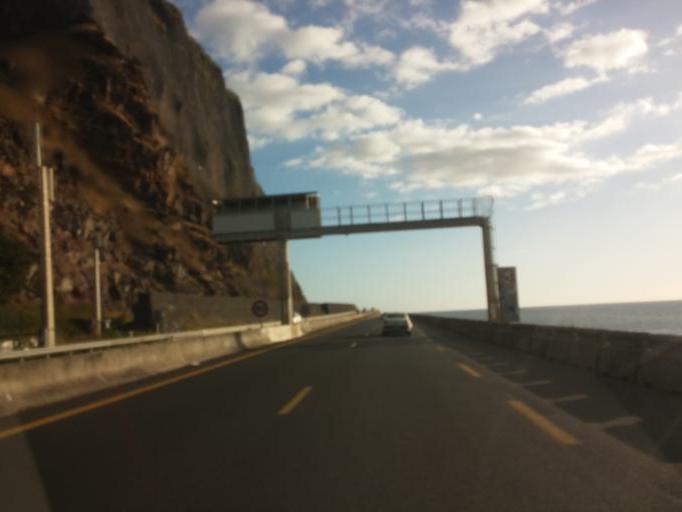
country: RE
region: Reunion
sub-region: Reunion
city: La Possession
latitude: -20.8970
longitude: 55.3744
